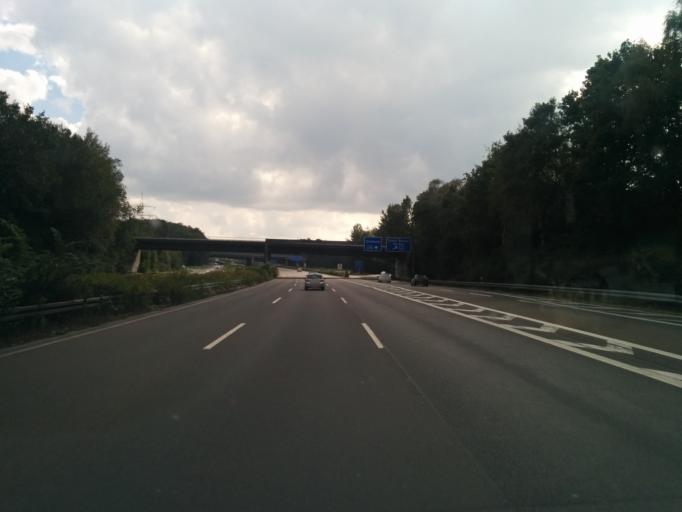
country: DE
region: North Rhine-Westphalia
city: Witten
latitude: 51.5020
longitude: 7.3860
